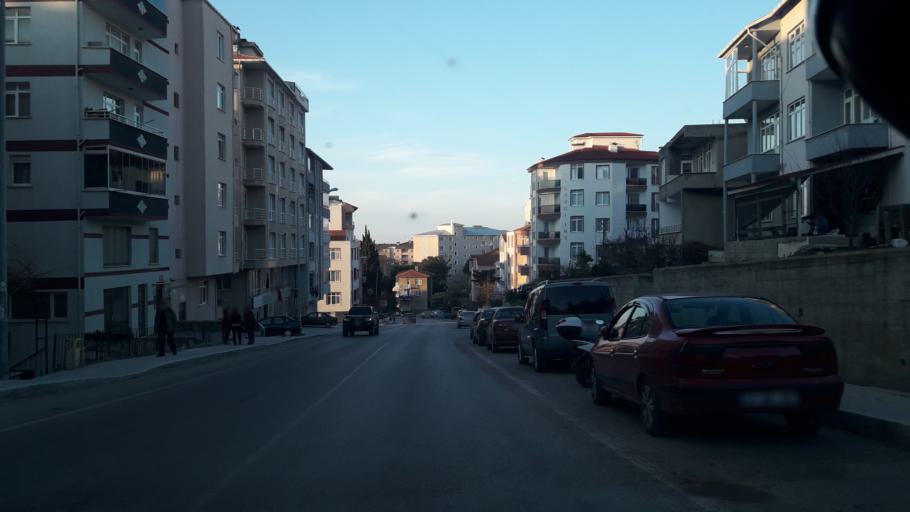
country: TR
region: Sinop
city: Sinop
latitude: 42.0257
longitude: 35.1611
